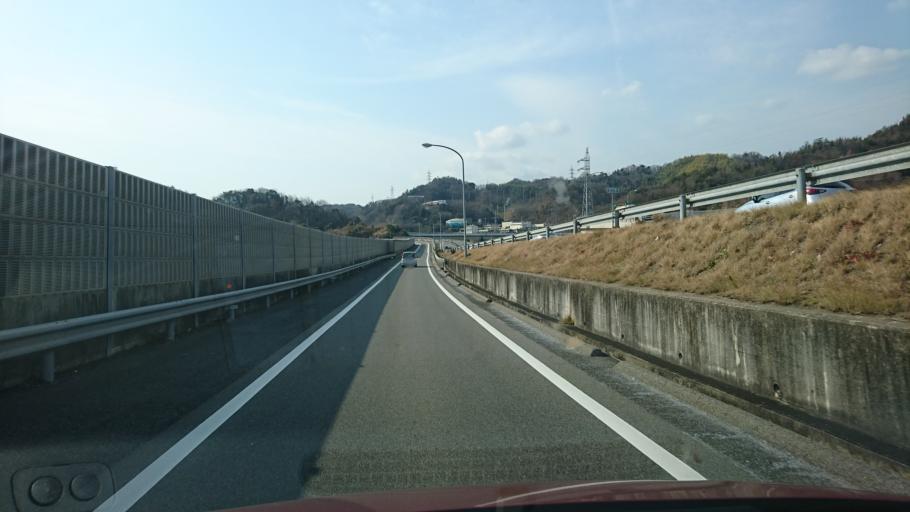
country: JP
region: Hiroshima
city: Onomichi
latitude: 34.4333
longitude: 133.2210
